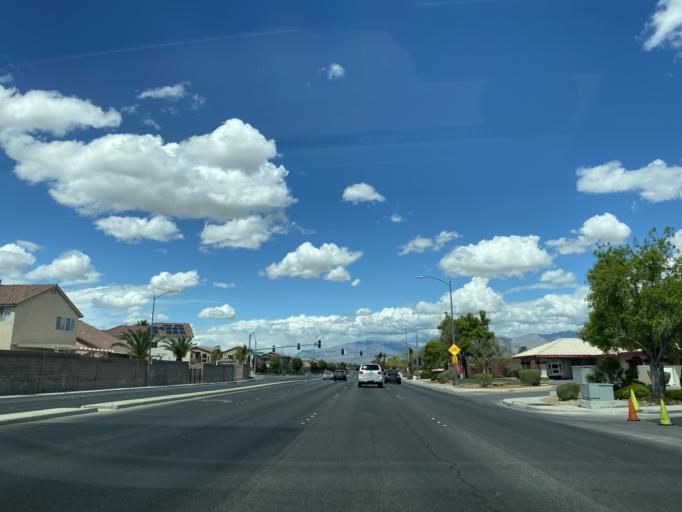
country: US
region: Nevada
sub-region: Clark County
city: Spring Valley
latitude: 36.2245
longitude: -115.2605
